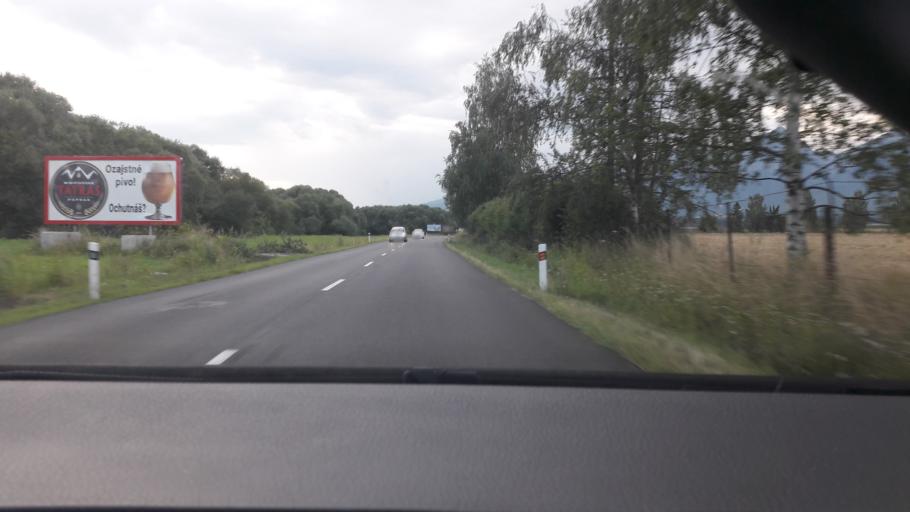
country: SK
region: Presovsky
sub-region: Okres Poprad
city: Poprad
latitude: 49.0679
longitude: 20.2632
